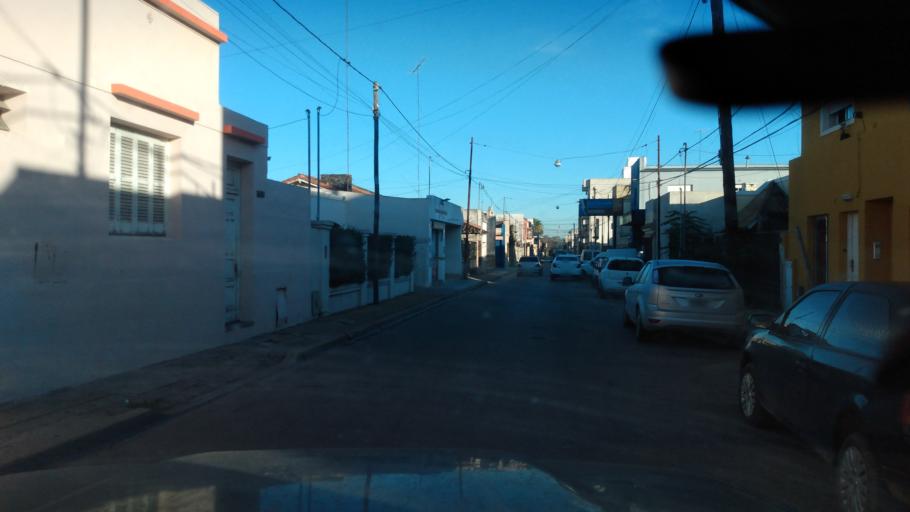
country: AR
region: Buenos Aires
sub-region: Partido de Lujan
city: Lujan
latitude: -34.5625
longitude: -59.1121
